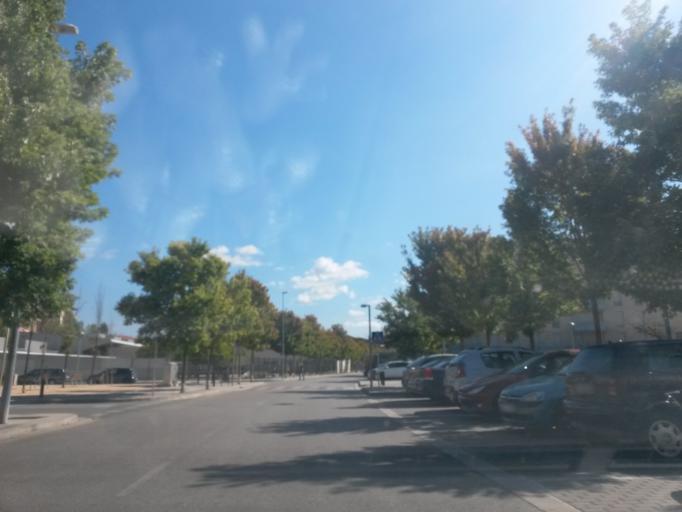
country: ES
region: Catalonia
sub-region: Provincia de Girona
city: Salt
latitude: 41.9727
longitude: 2.7984
